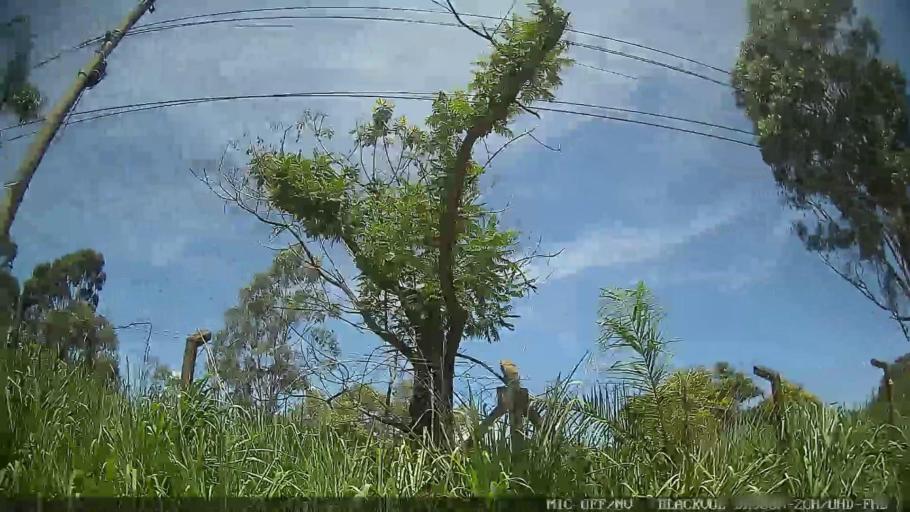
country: BR
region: Sao Paulo
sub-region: Jaguariuna
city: Jaguariuna
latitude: -22.7497
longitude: -47.0010
